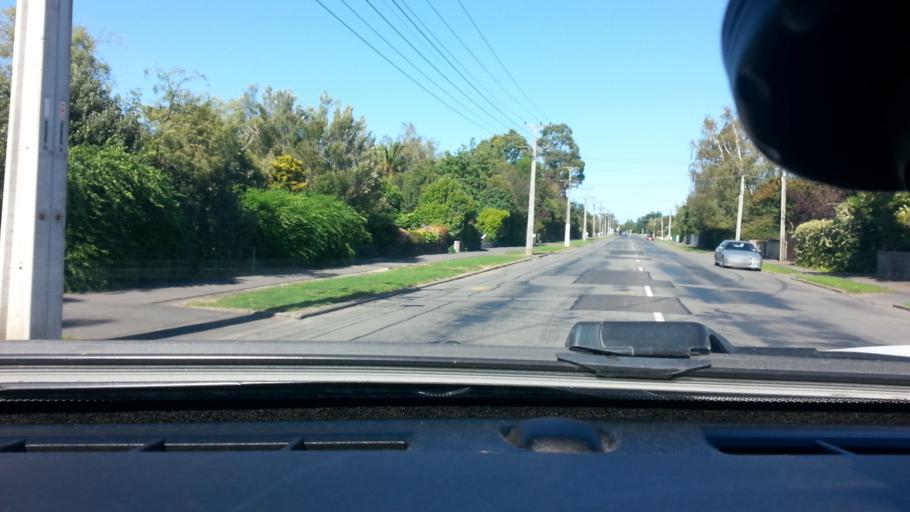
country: NZ
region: Wellington
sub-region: Masterton District
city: Masterton
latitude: -40.9657
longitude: 175.6391
